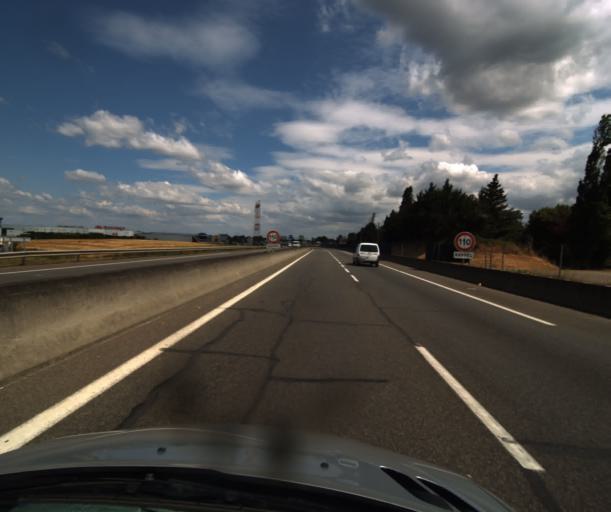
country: FR
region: Midi-Pyrenees
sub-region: Departement du Tarn-et-Garonne
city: Bressols
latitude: 43.9835
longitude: 1.3353
